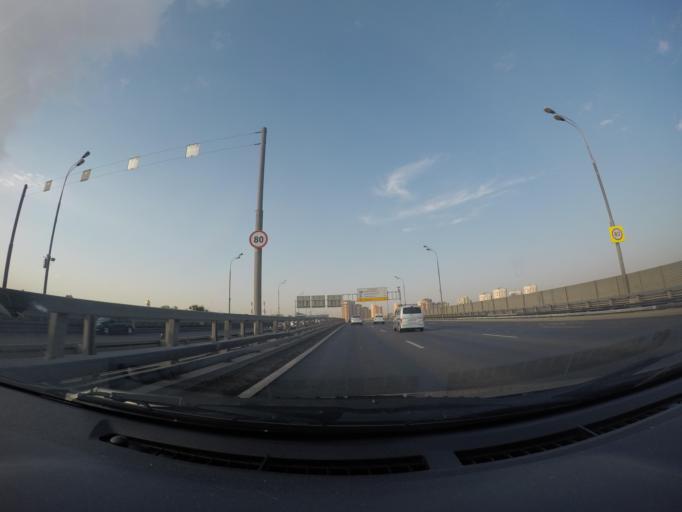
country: RU
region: Moscow
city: Lefortovo
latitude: 55.7434
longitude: 37.6994
